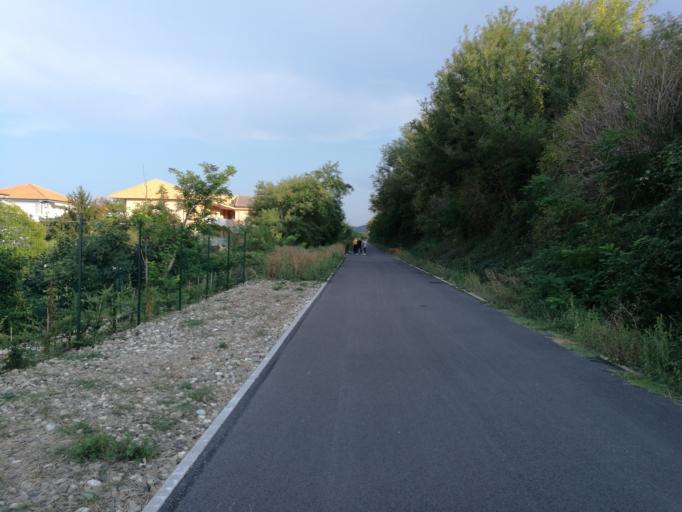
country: IT
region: Abruzzo
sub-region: Provincia di Chieti
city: Fossacesia
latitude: 42.2477
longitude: 14.5141
